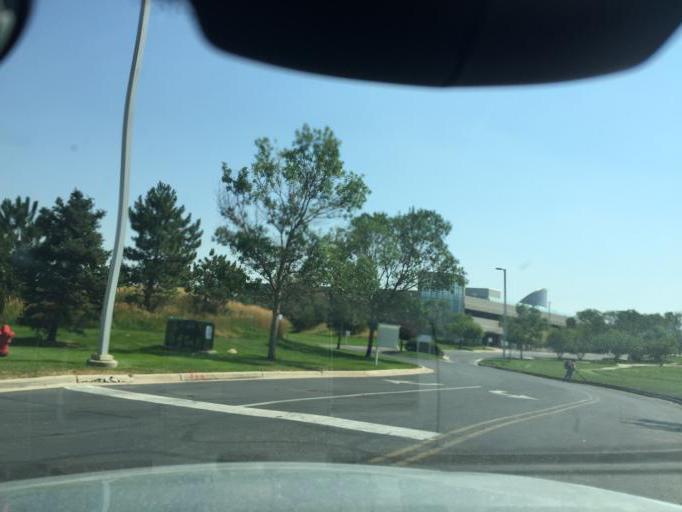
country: US
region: Colorado
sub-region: Adams County
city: Northglenn
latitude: 39.9121
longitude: -105.0060
